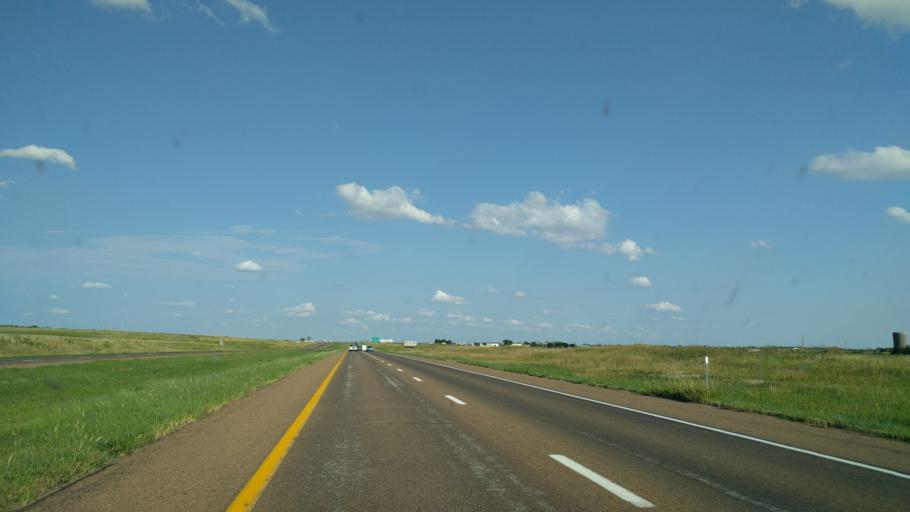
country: US
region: Kansas
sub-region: Ellis County
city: Hays
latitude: 38.9187
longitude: -99.3729
